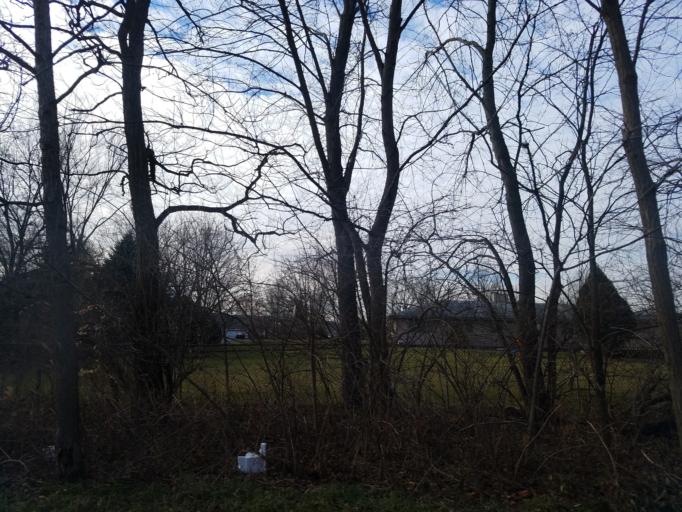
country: US
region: Illinois
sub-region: Will County
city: Homer Glen
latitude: 41.5696
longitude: -87.9436
